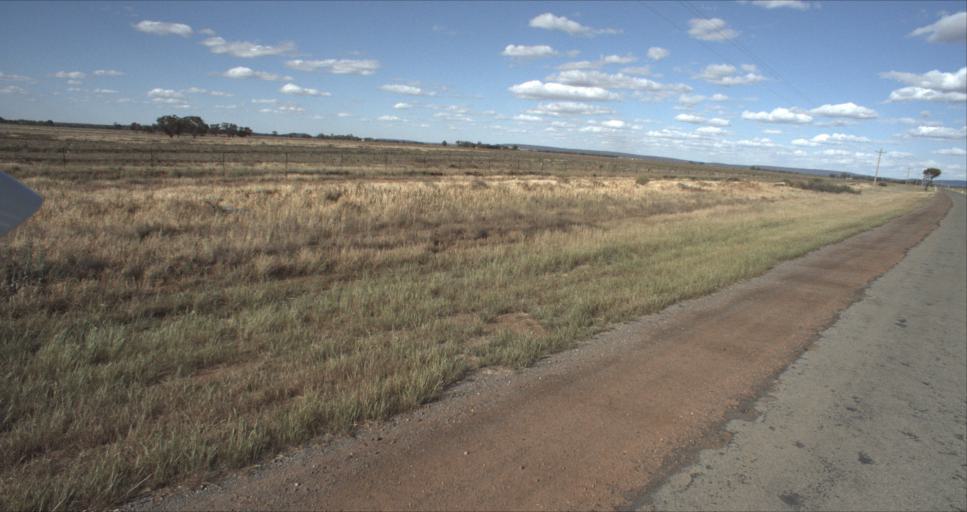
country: AU
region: New South Wales
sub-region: Leeton
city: Leeton
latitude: -34.4566
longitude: 146.2874
